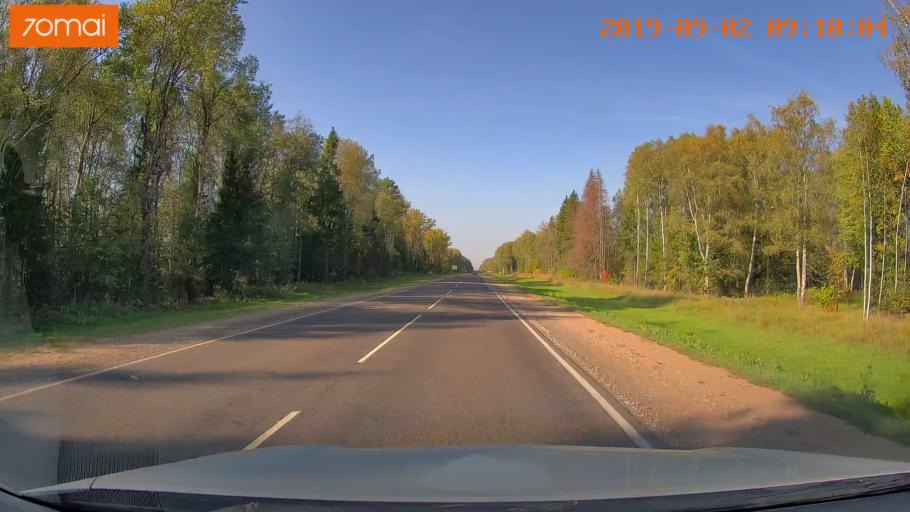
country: RU
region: Kaluga
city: Myatlevo
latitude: 54.8791
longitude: 35.6090
